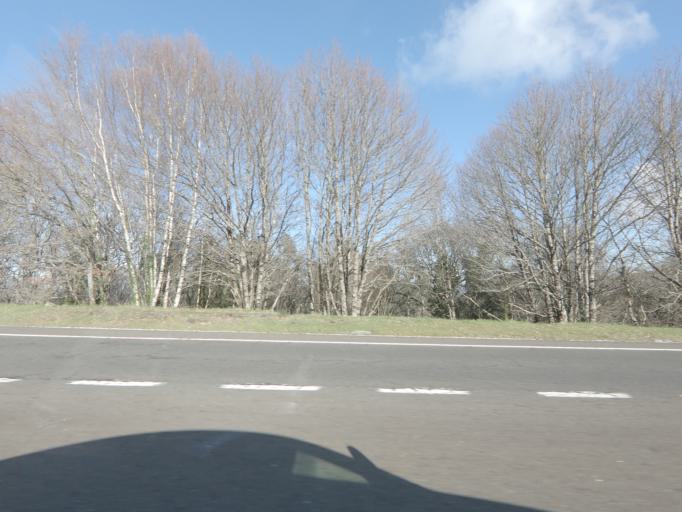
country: ES
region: Galicia
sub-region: Provincia de Pontevedra
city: Silleda
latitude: 42.6997
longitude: -8.3389
